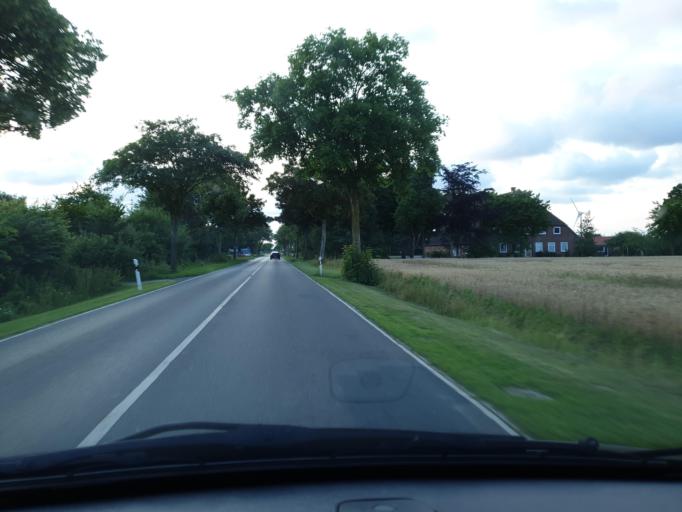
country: DE
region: Schleswig-Holstein
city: Kronprinzenkoog
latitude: 53.9729
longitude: 8.9240
